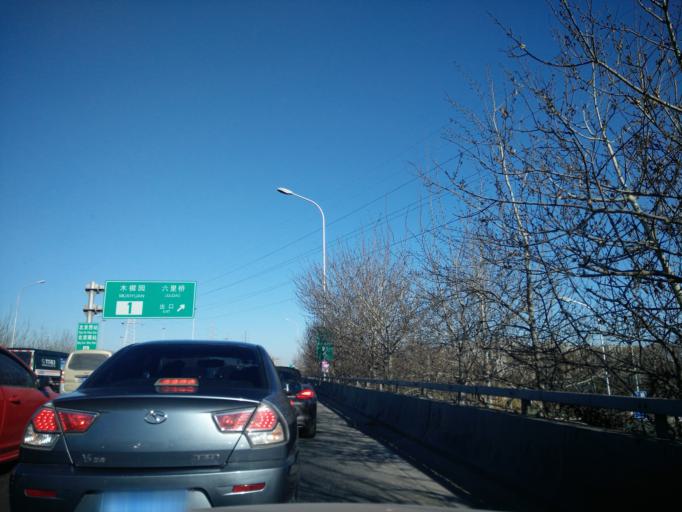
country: CN
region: Beijing
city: Huaxiang
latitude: 39.8445
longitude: 116.3400
